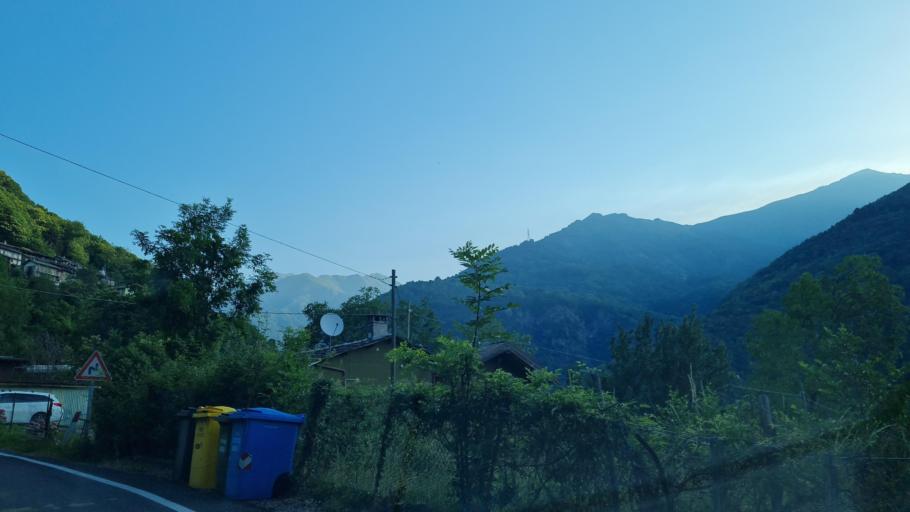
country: IT
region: Piedmont
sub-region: Provincia di Torino
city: Pont-Canavese
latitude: 45.4338
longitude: 7.5861
